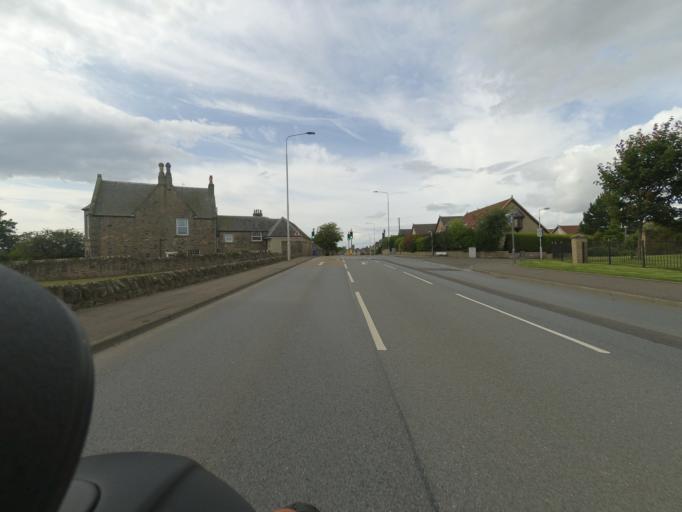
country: GB
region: Scotland
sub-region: Fife
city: Anstruther
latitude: 56.2261
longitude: -2.6961
